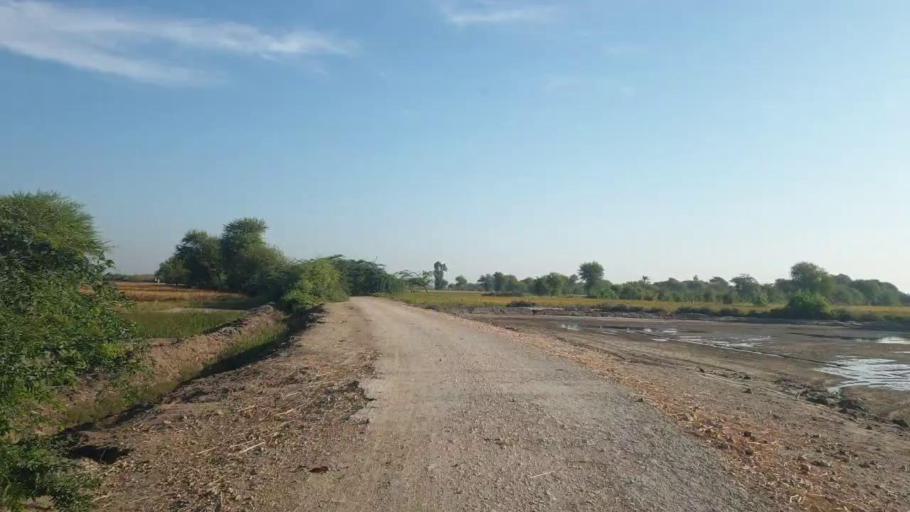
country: PK
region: Sindh
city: Talhar
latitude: 24.8244
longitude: 68.8397
